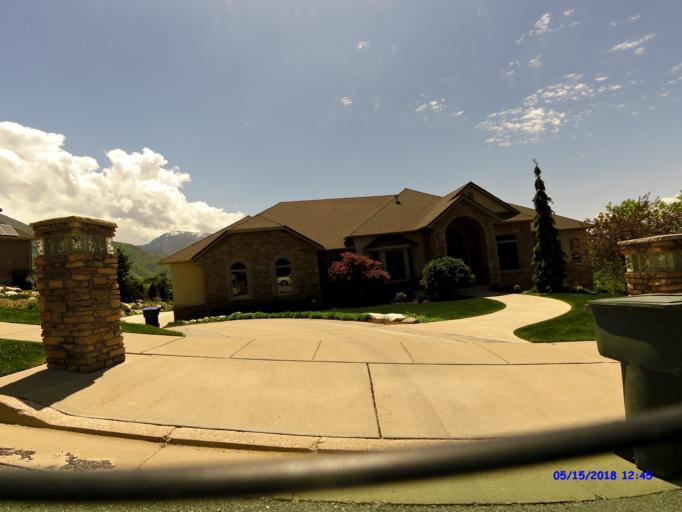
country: US
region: Utah
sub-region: Weber County
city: Uintah
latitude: 41.1618
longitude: -111.9242
